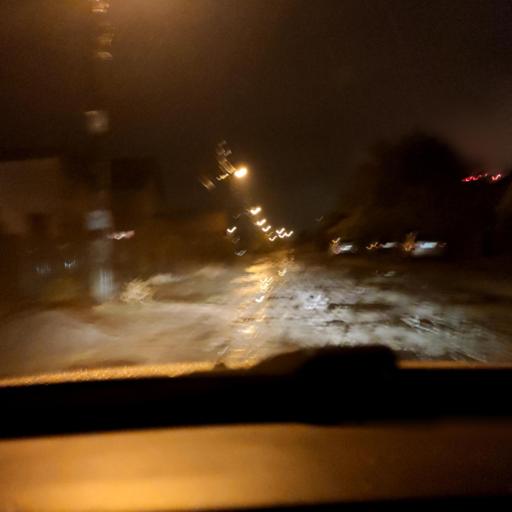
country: RU
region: Voronezj
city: Somovo
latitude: 51.7409
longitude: 39.3231
